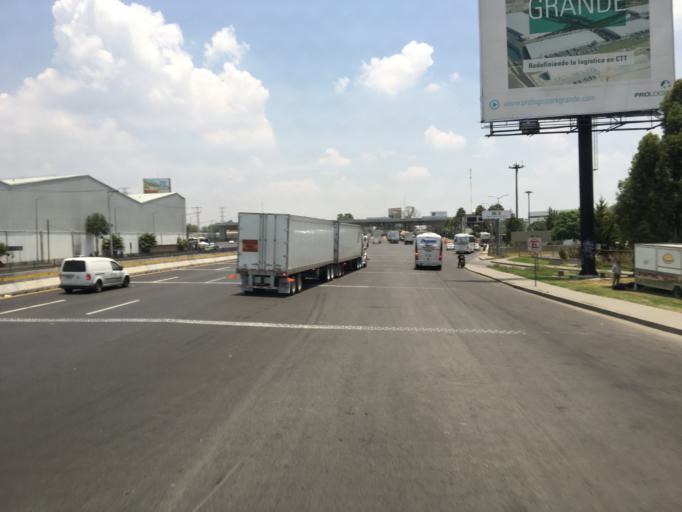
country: MX
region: Mexico
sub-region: Cuautitlan
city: San Jose del Puente
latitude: 19.7128
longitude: -99.2069
